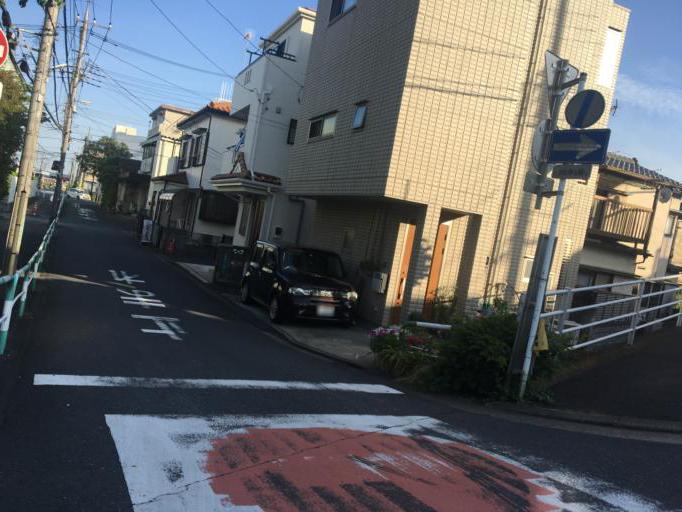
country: JP
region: Saitama
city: Shiki
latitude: 35.8433
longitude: 139.6206
